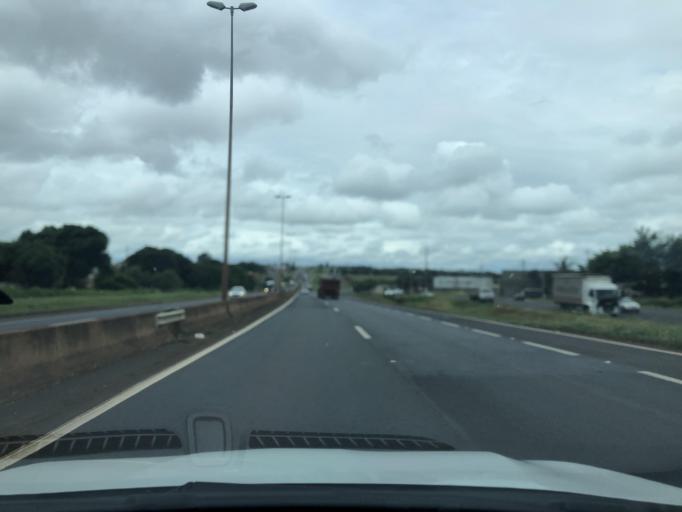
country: BR
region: Minas Gerais
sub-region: Uberaba
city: Uberaba
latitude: -19.7794
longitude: -47.9682
